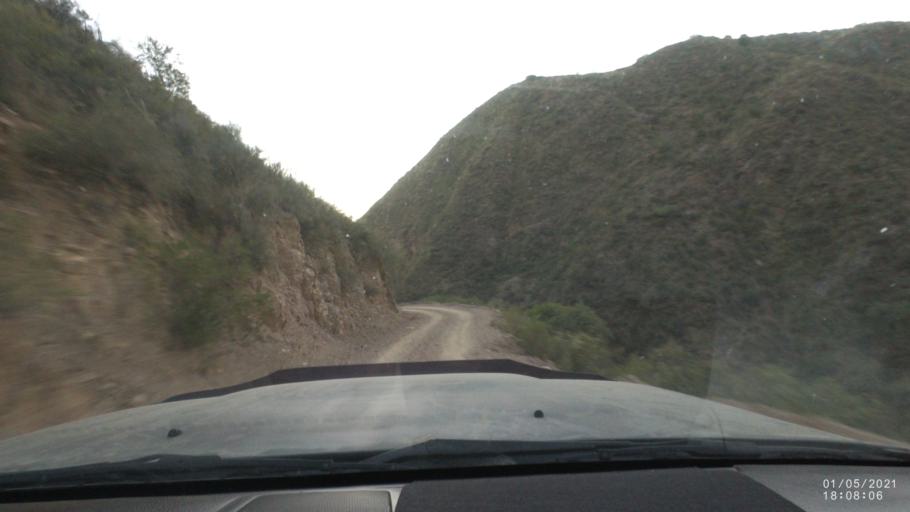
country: BO
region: Cochabamba
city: Capinota
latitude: -17.6847
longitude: -66.1895
